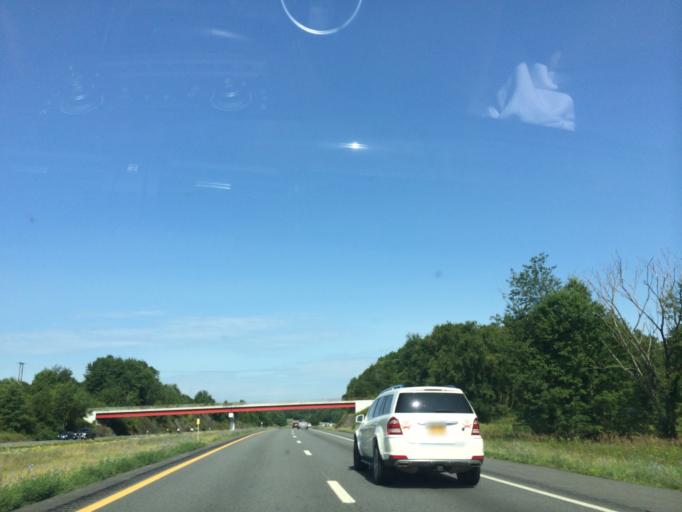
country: US
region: New York
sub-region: Orange County
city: Walden
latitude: 41.5135
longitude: -74.1554
